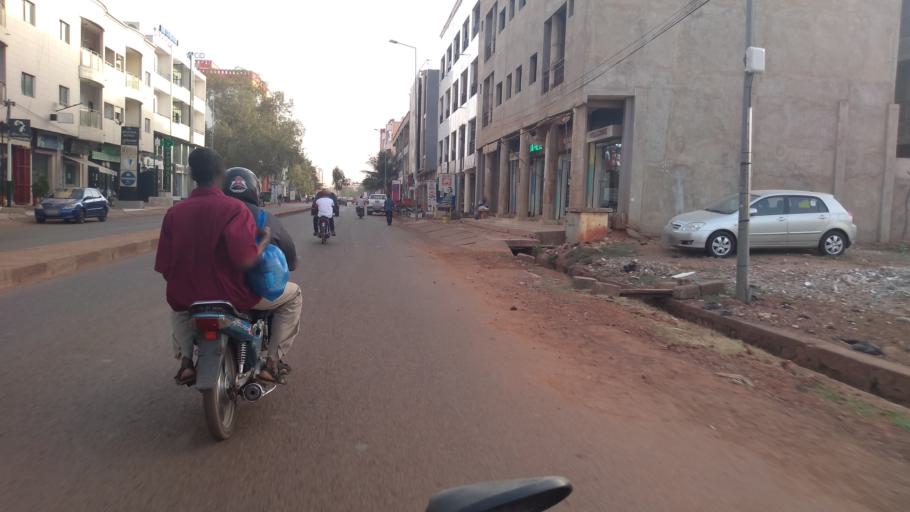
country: ML
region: Bamako
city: Bamako
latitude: 12.6286
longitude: -8.0323
